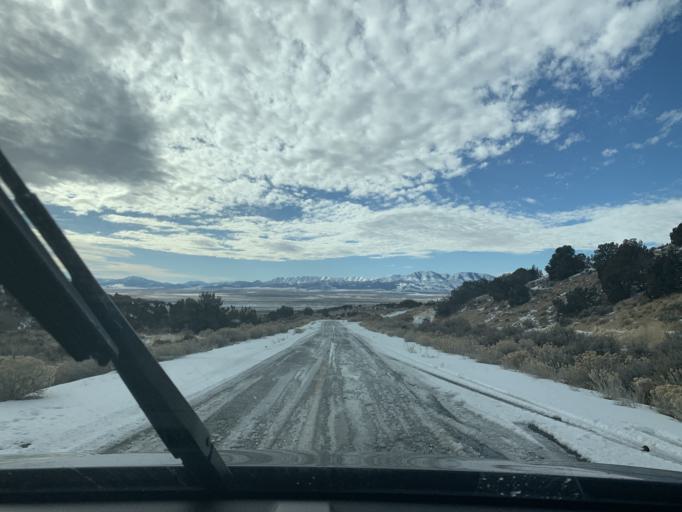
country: US
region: Utah
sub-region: Tooele County
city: Tooele
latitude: 40.3073
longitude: -112.2563
